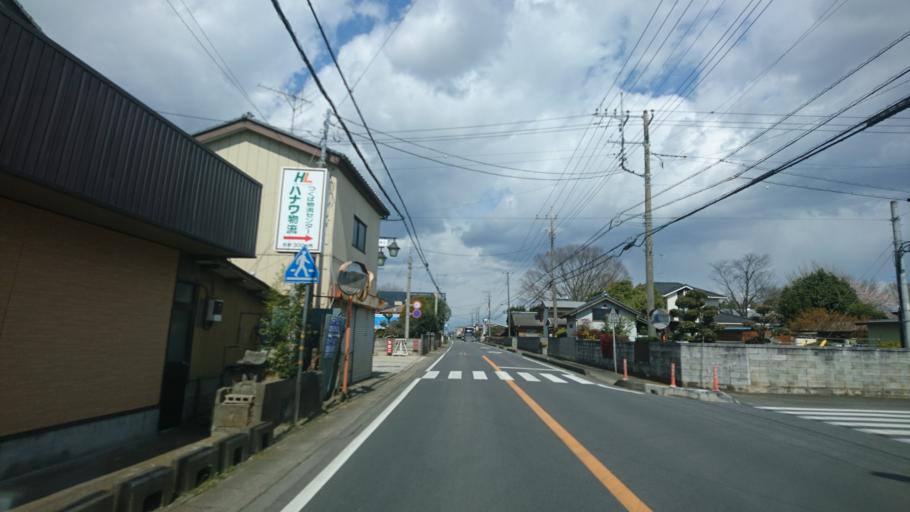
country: JP
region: Ibaraki
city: Ishige
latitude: 36.2097
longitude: 139.9390
